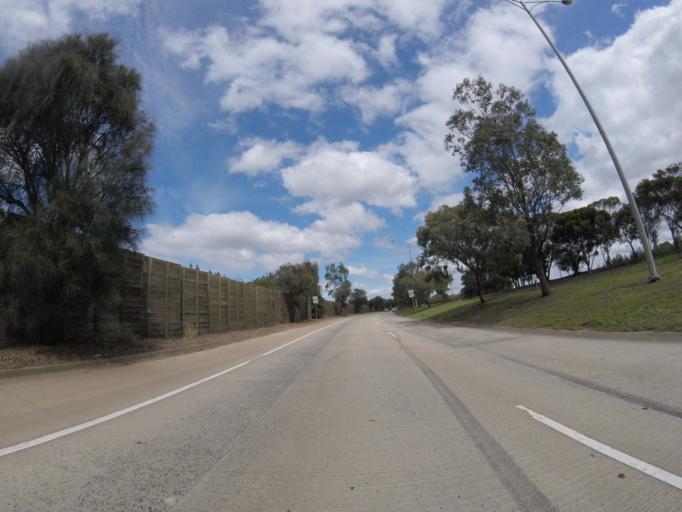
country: AU
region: Victoria
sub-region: Brimbank
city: Keilor Park
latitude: -37.7155
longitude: 144.8588
